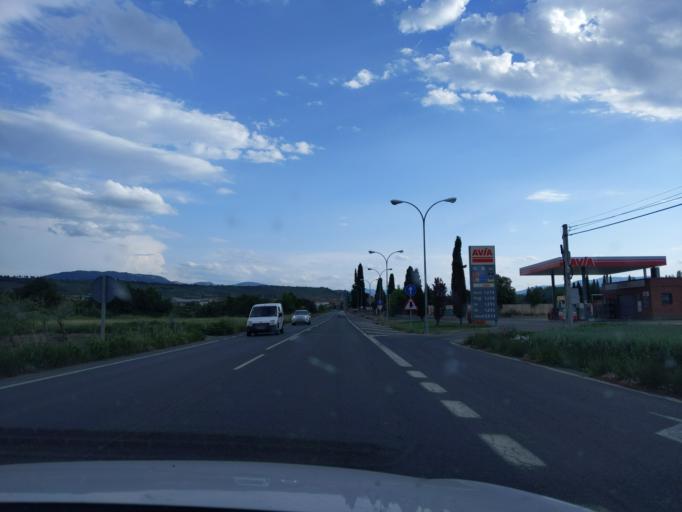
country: ES
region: La Rioja
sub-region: Provincia de La Rioja
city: Alberite
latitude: 42.4136
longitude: -2.4347
